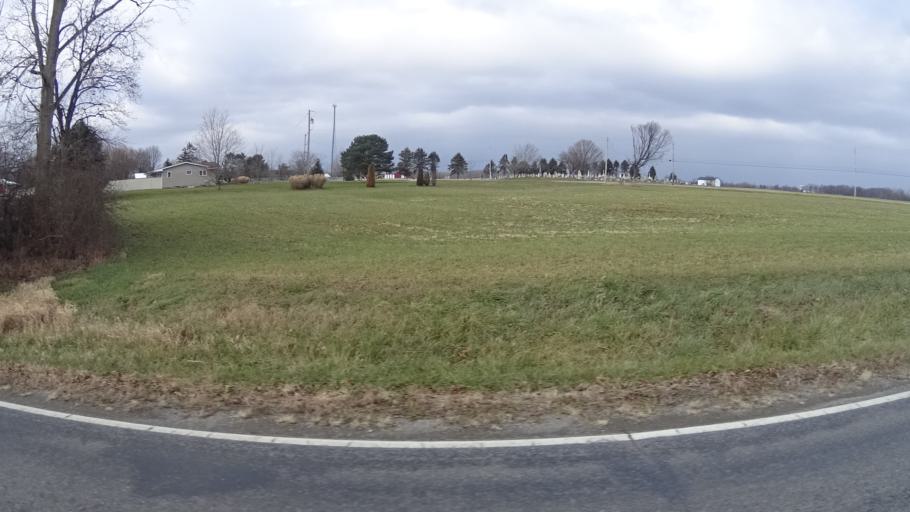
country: US
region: Ohio
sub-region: Lorain County
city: Oberlin
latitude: 41.2360
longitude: -82.2114
